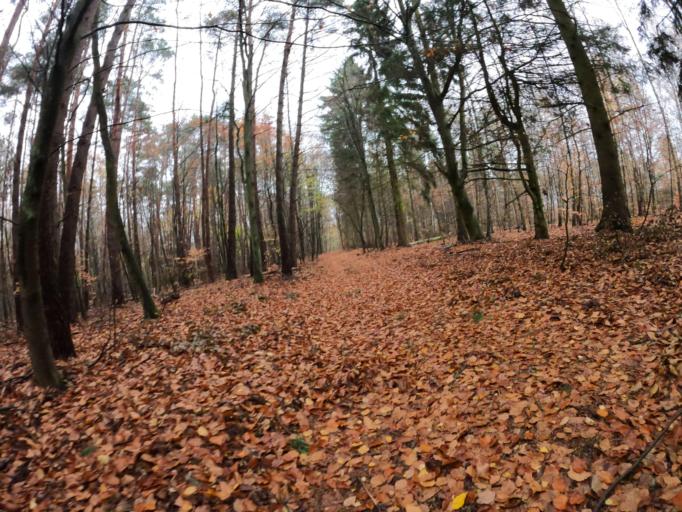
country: PL
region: West Pomeranian Voivodeship
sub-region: Powiat walecki
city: Tuczno
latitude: 53.2646
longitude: 16.2588
